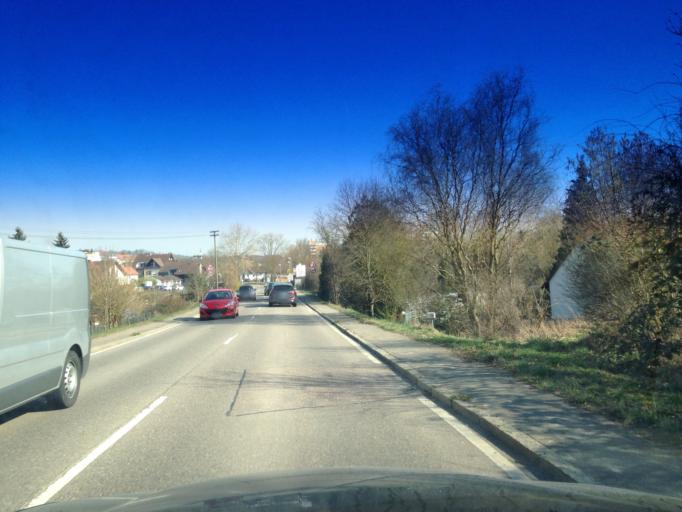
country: DE
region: Baden-Wuerttemberg
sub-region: Regierungsbezirk Stuttgart
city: Vaihingen an der Enz
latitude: 48.9299
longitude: 8.9516
